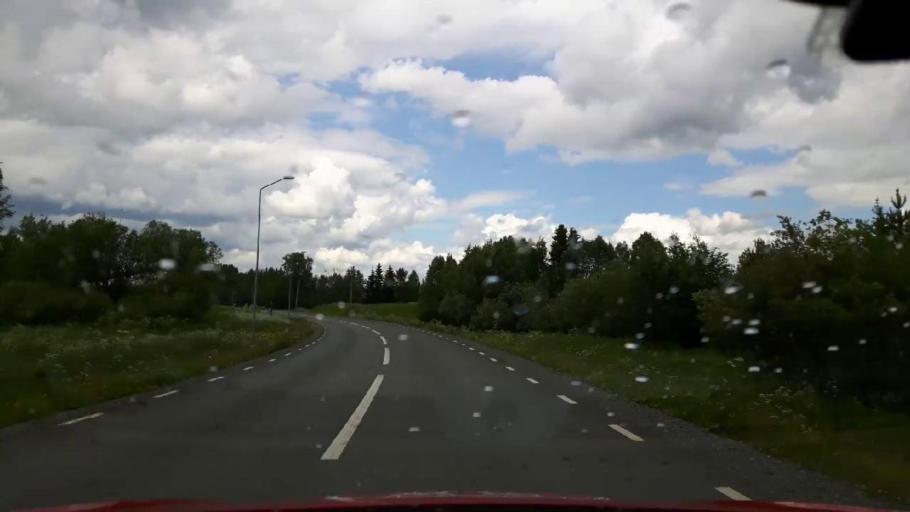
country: SE
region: Jaemtland
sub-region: Krokoms Kommun
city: Krokom
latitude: 63.5513
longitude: 14.2805
